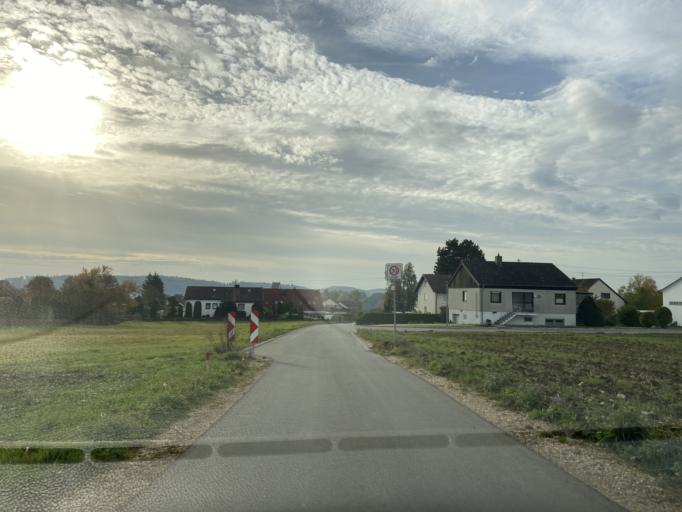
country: DE
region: Baden-Wuerttemberg
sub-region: Tuebingen Region
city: Bingen
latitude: 48.1154
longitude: 9.2735
